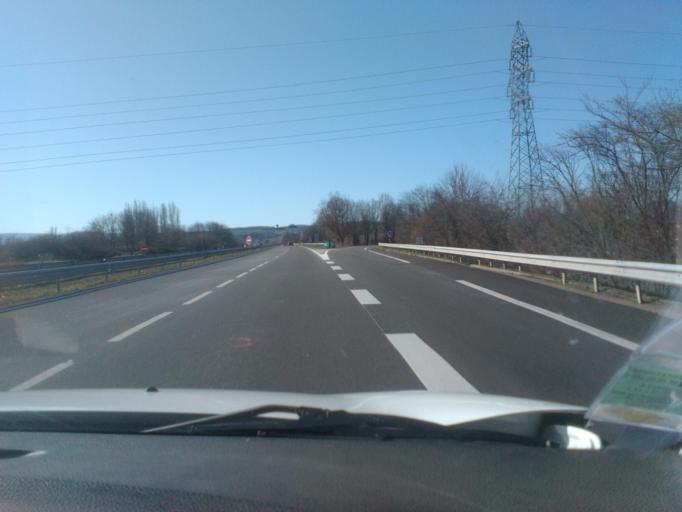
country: FR
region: Alsace
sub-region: Departement du Bas-Rhin
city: Dorlisheim
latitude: 48.5204
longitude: 7.5022
